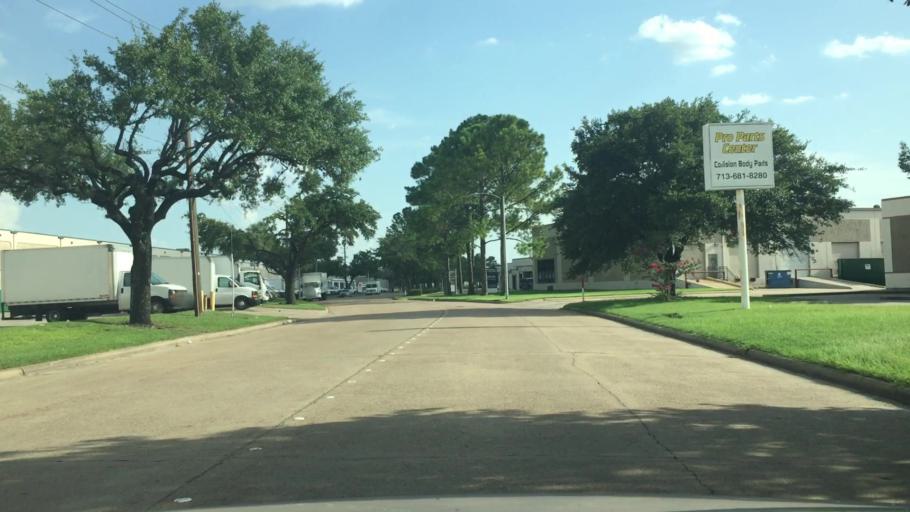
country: US
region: Texas
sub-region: Harris County
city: Spring Valley
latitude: 29.8117
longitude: -95.4677
